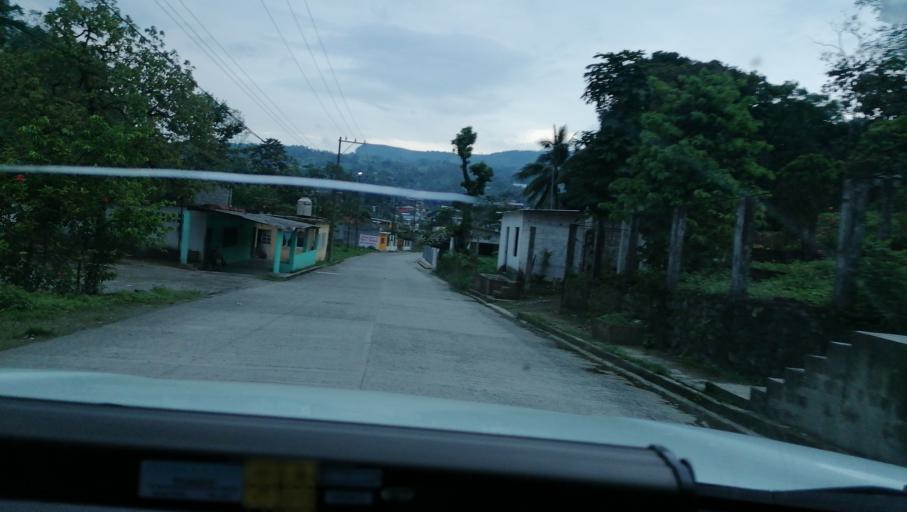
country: MX
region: Chiapas
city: Ixtacomitan
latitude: 17.4281
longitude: -93.1017
